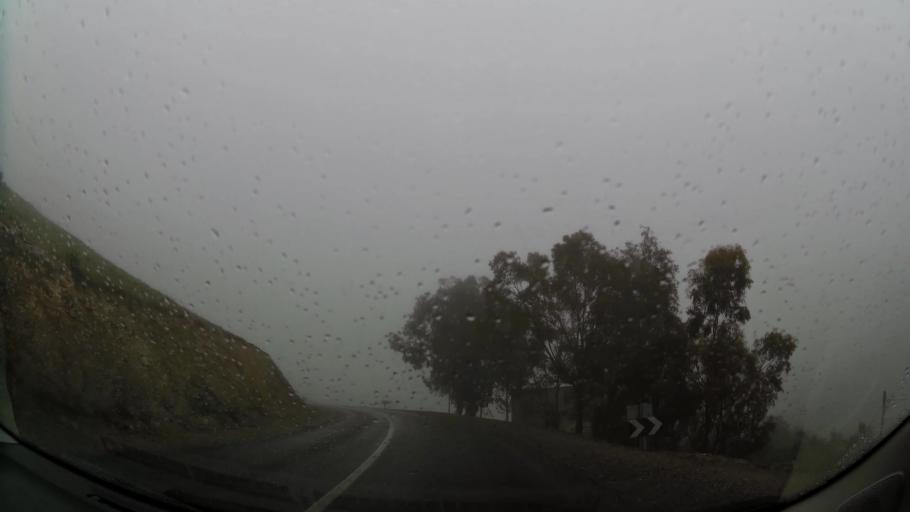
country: MA
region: Oriental
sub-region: Nador
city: Boudinar
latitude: 35.0941
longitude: -3.5322
